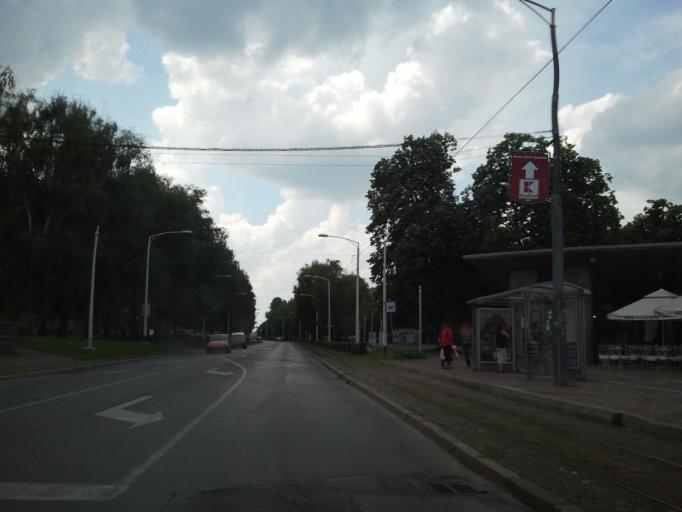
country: HR
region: Osjecko-Baranjska
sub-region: Grad Osijek
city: Osijek
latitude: 45.5550
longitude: 18.7201
